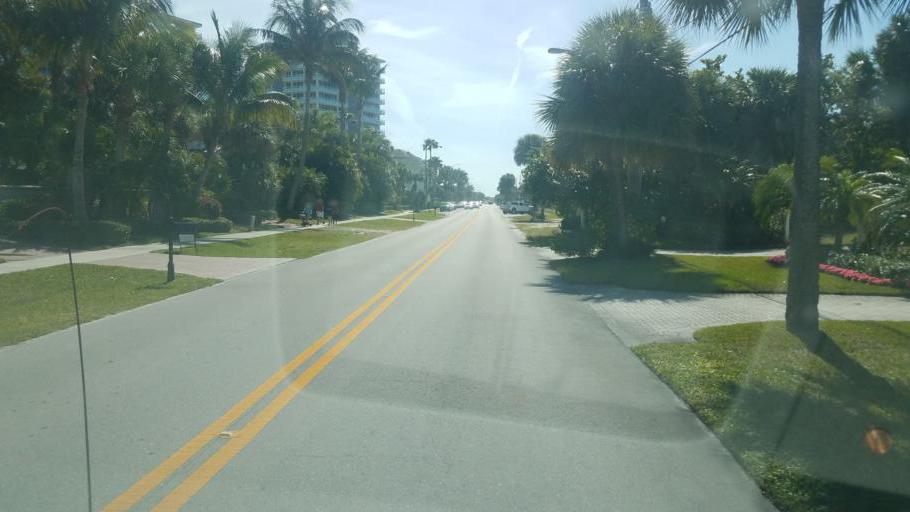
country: US
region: Florida
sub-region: Indian River County
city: Vero Beach
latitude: 27.6579
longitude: -80.3579
